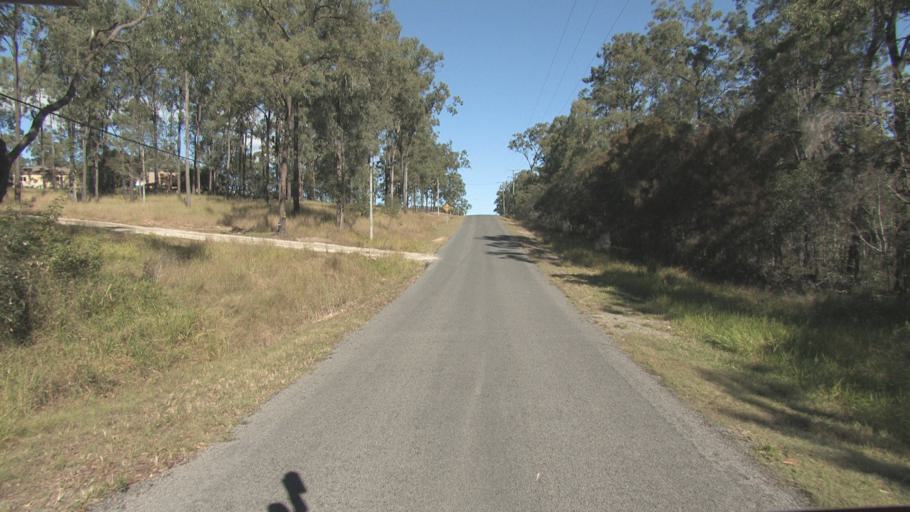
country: AU
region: Queensland
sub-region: Logan
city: Chambers Flat
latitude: -27.8138
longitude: 153.0778
